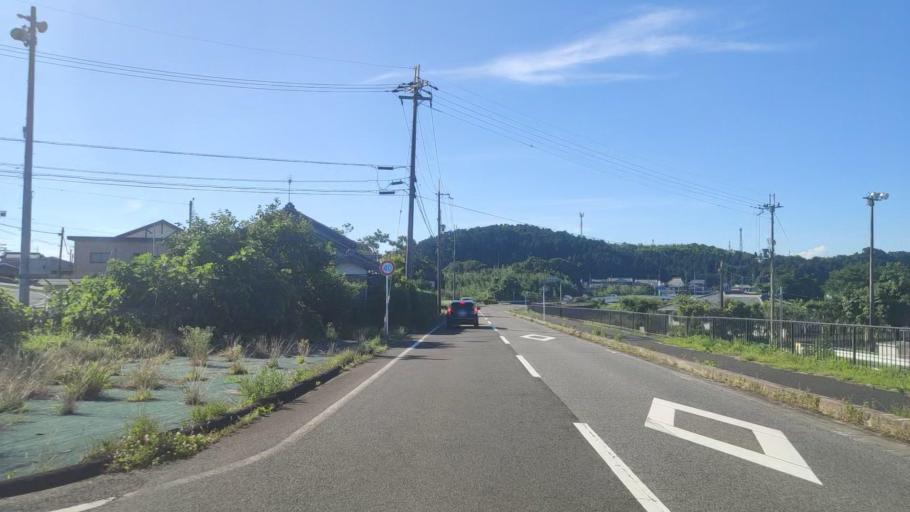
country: JP
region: Shiga Prefecture
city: Minakuchicho-matoba
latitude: 34.9544
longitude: 136.2026
